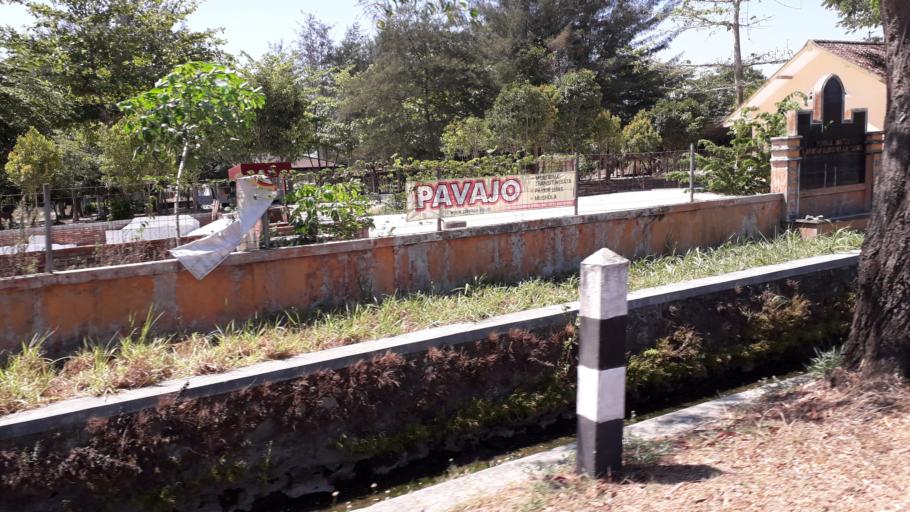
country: ID
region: Daerah Istimewa Yogyakarta
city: Pundong
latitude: -7.9428
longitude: 110.3328
